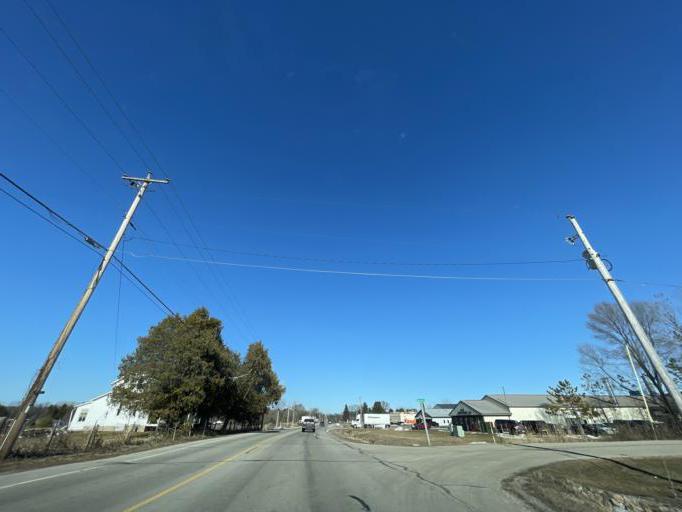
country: US
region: Wisconsin
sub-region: Brown County
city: Suamico
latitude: 44.6272
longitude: -88.0591
